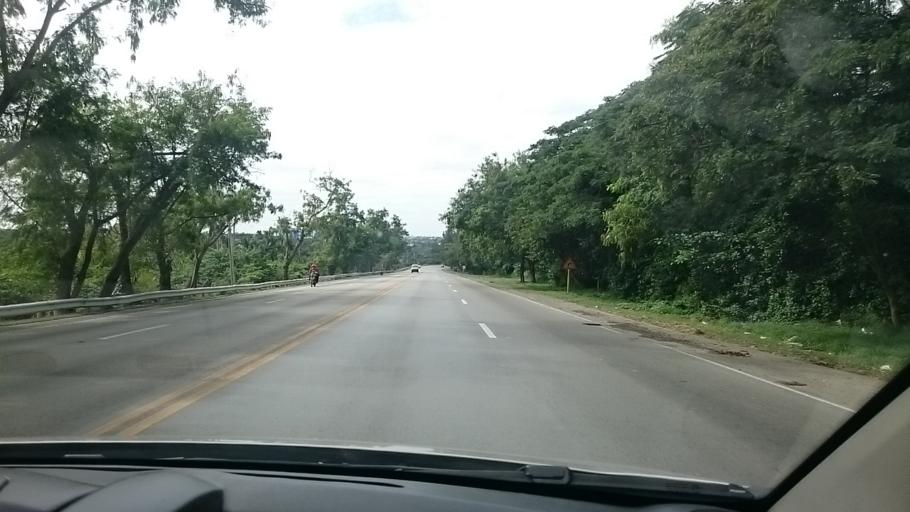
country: CU
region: La Habana
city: Alamar
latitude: 23.1484
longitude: -82.2792
